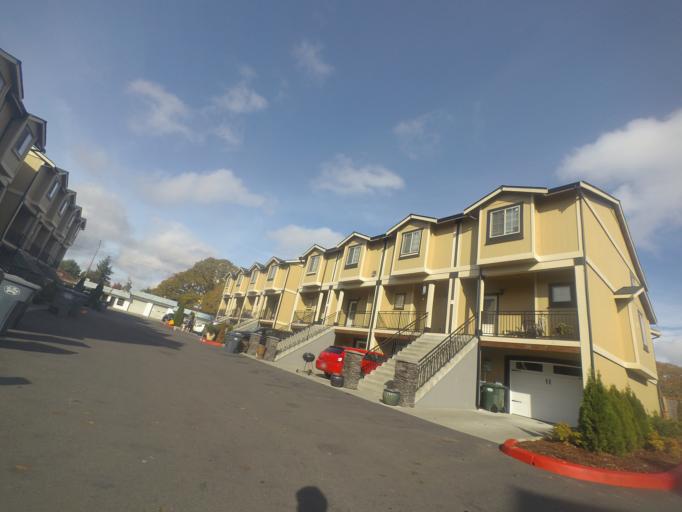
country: US
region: Washington
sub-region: Pierce County
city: Lakewood
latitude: 47.1752
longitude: -122.5106
